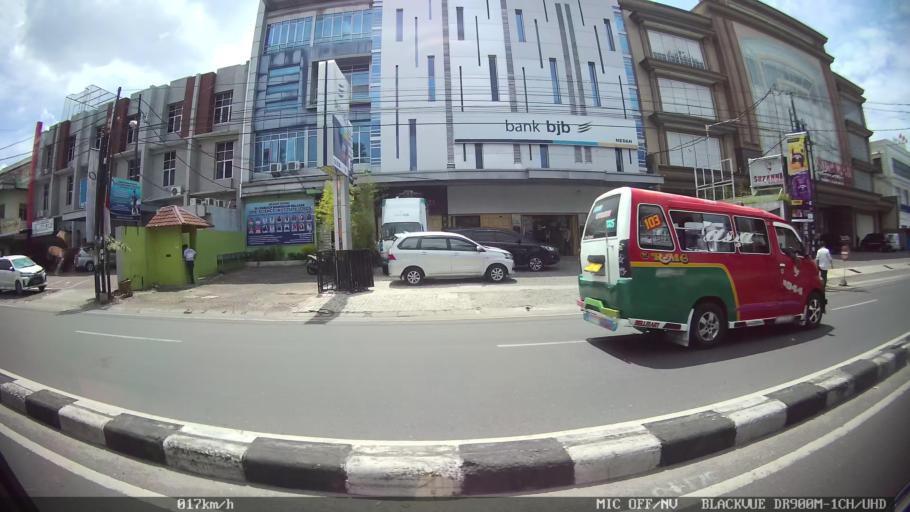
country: ID
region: North Sumatra
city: Medan
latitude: 3.5752
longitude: 98.6608
